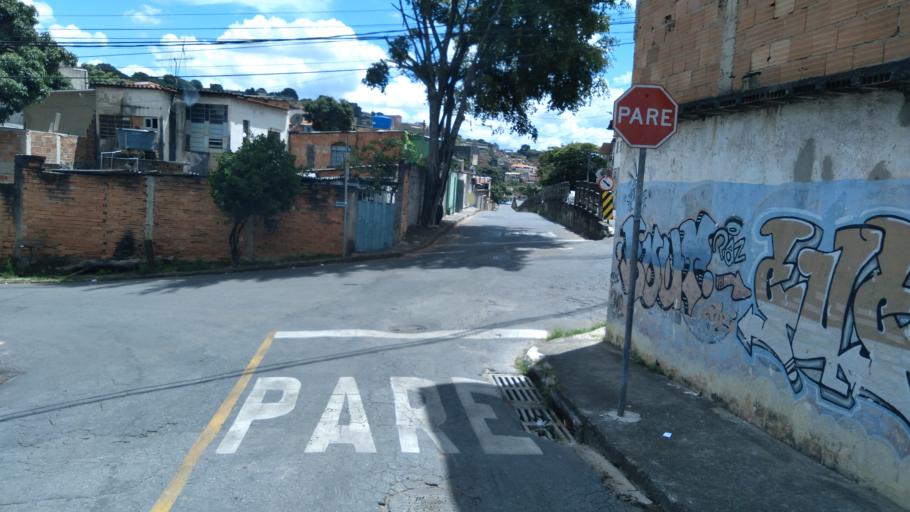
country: BR
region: Minas Gerais
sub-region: Belo Horizonte
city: Belo Horizonte
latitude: -19.8674
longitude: -43.9116
